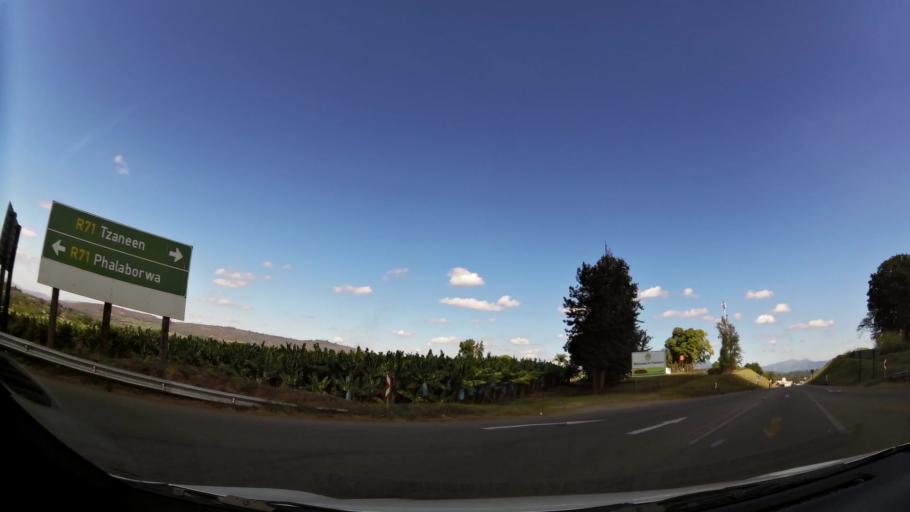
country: ZA
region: Limpopo
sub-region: Mopani District Municipality
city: Tzaneen
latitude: -23.8143
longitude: 30.1733
